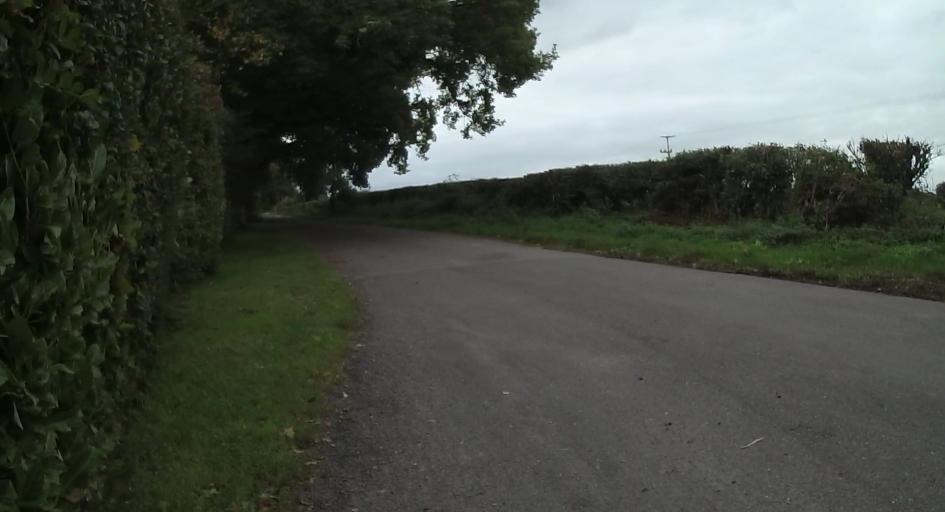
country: GB
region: England
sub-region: Hampshire
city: Four Marks
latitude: 51.1155
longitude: -1.0863
